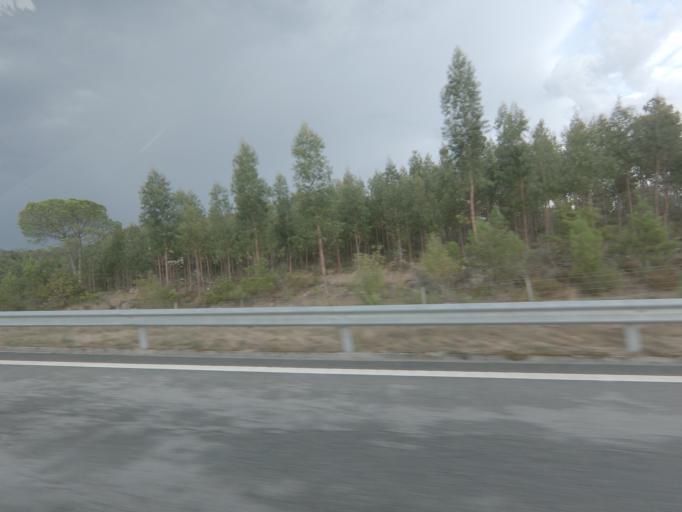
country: PT
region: Viseu
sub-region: Viseu
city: Abraveses
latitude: 40.6825
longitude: -7.9679
